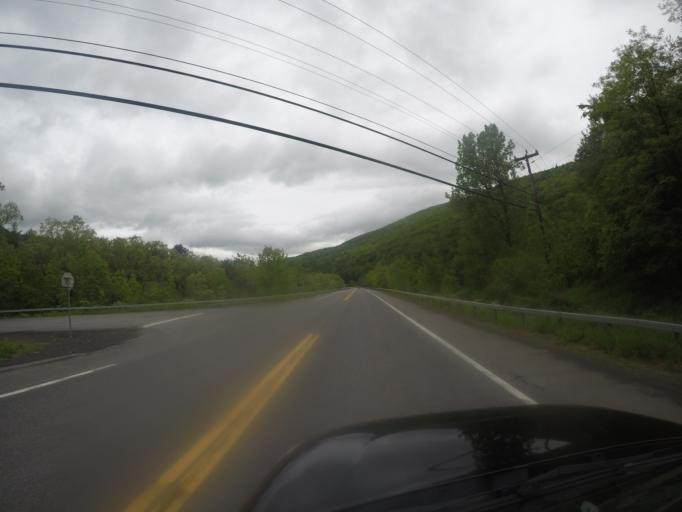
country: US
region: New York
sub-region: Ulster County
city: Shokan
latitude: 42.0880
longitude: -74.3326
